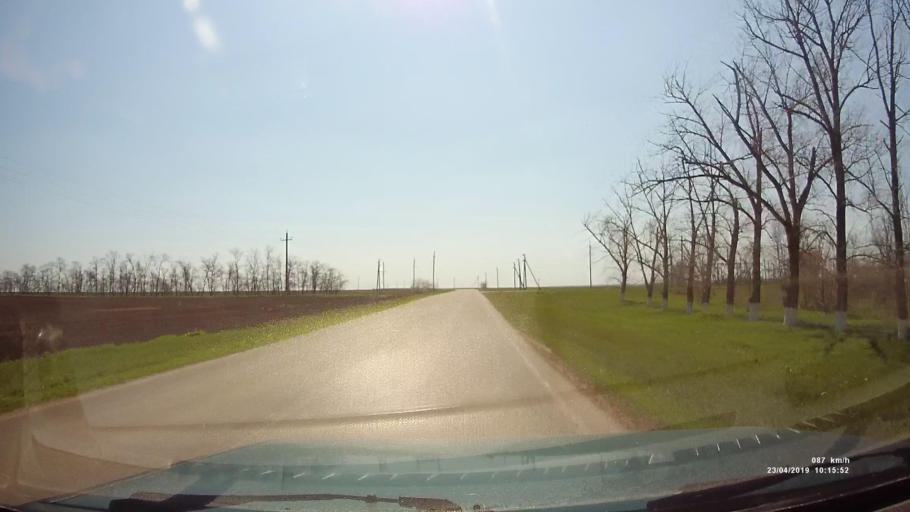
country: RU
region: Rostov
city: Sovetskoye
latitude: 46.6625
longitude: 42.3865
